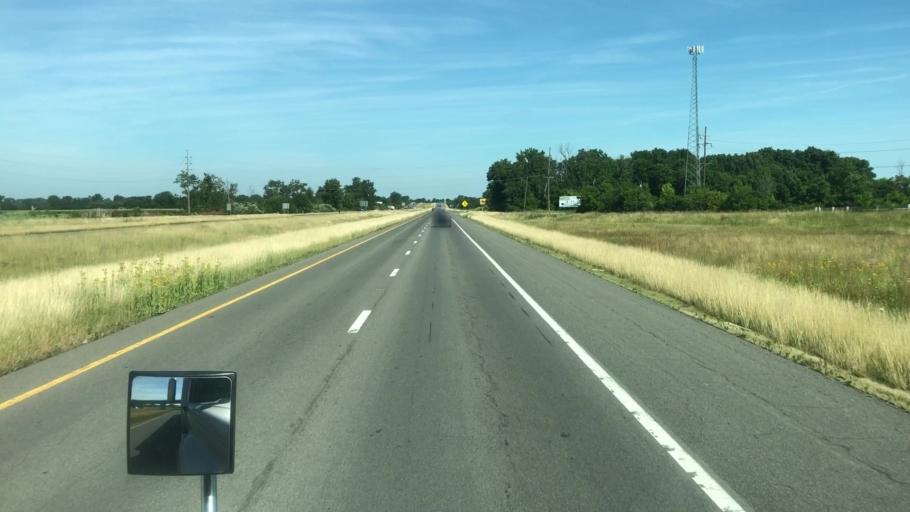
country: US
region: Ohio
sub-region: Erie County
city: Sandusky
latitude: 41.4190
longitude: -82.7595
